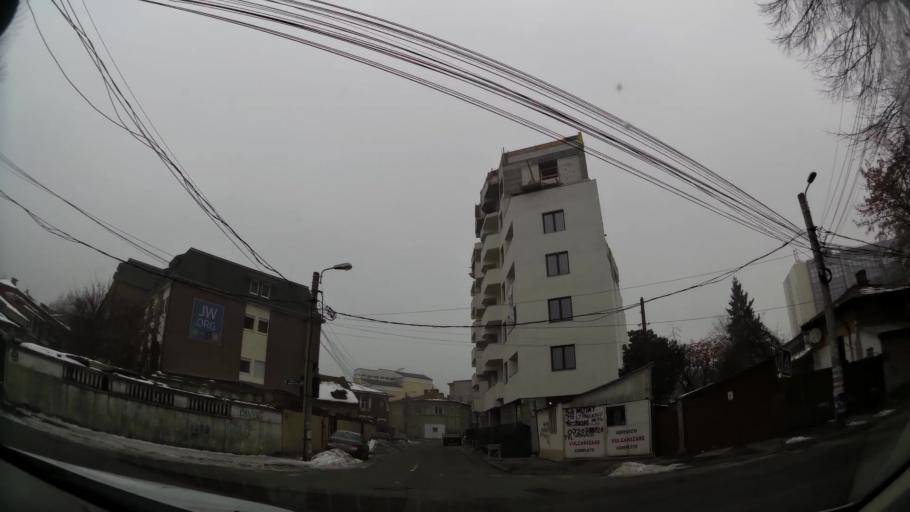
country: RO
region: Bucuresti
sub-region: Municipiul Bucuresti
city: Bucharest
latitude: 44.4339
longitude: 26.1323
